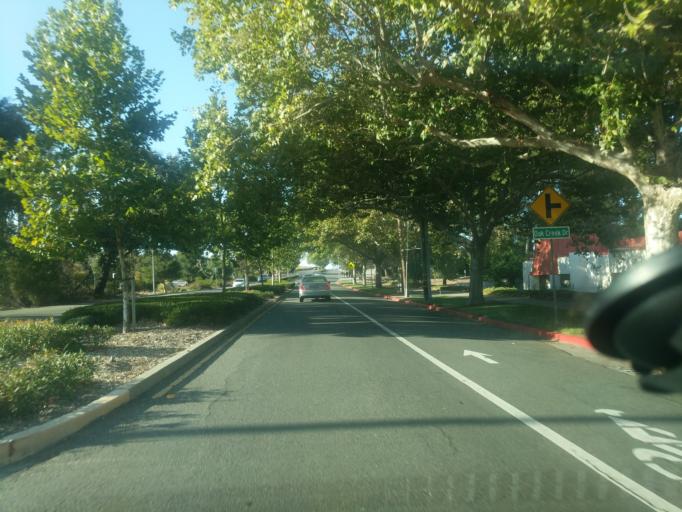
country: US
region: California
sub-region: Alameda County
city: Dublin
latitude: 37.6722
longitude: -121.9202
